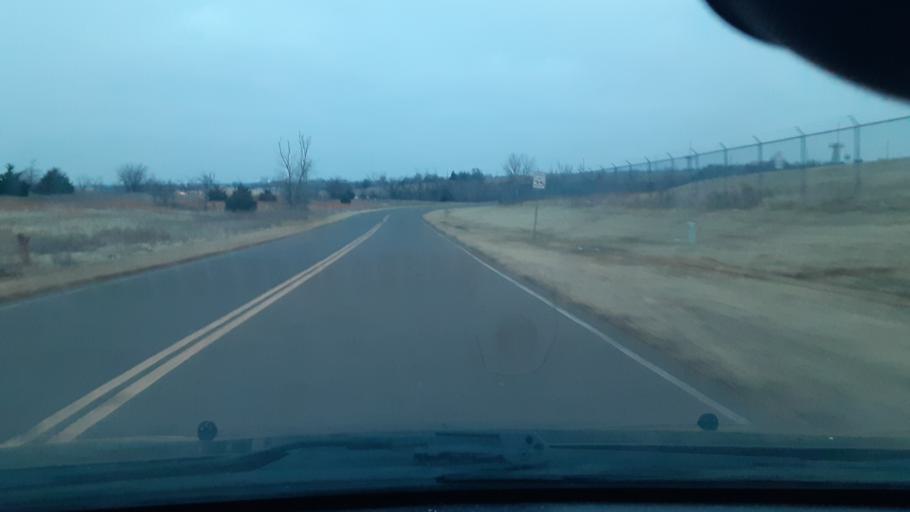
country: US
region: Oklahoma
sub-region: Logan County
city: Guthrie
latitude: 35.8592
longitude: -97.4205
